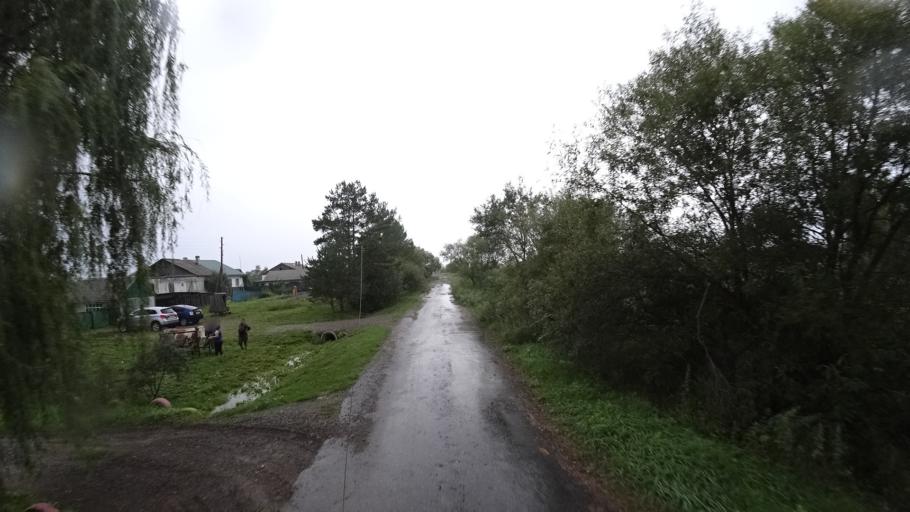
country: RU
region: Primorskiy
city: Chernigovka
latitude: 44.4086
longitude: 132.5326
